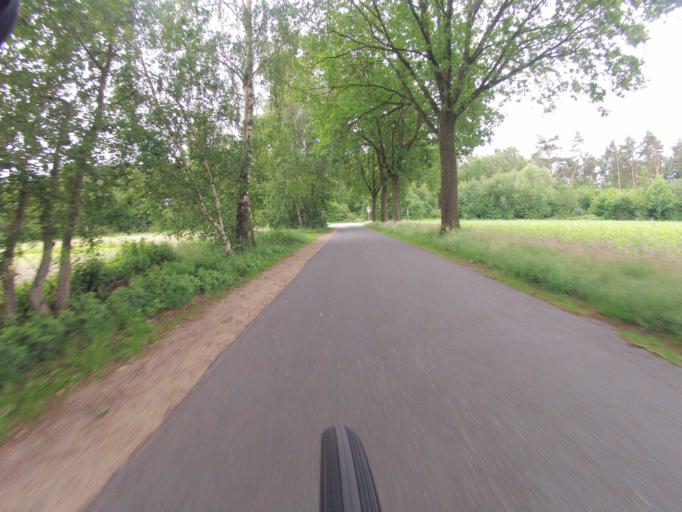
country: DE
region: North Rhine-Westphalia
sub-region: Regierungsbezirk Munster
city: Saerbeck
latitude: 52.1695
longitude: 7.6136
